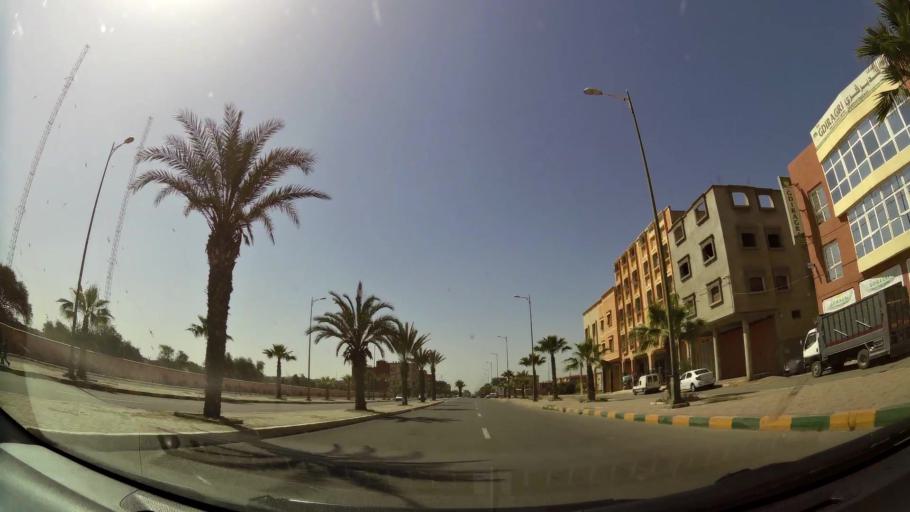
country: MA
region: Souss-Massa-Draa
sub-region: Inezgane-Ait Mellou
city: Inezgane
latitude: 30.3268
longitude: -9.5037
